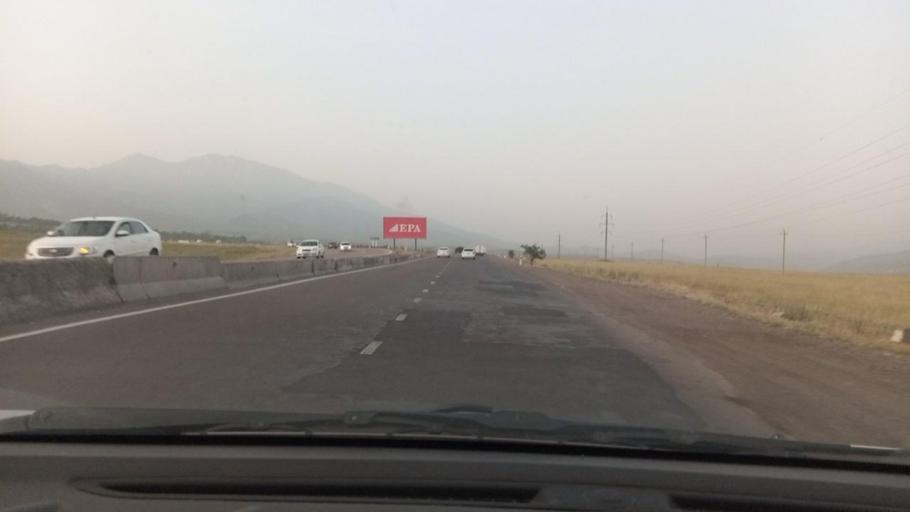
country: UZ
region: Toshkent
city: Angren
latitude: 41.0341
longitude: 70.1422
